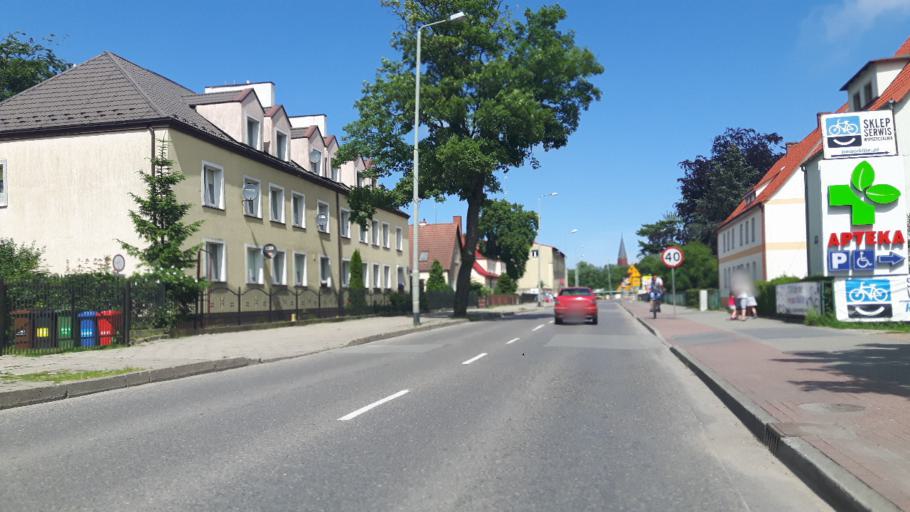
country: PL
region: Pomeranian Voivodeship
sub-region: Powiat slupski
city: Ustka
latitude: 54.5783
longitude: 16.8551
